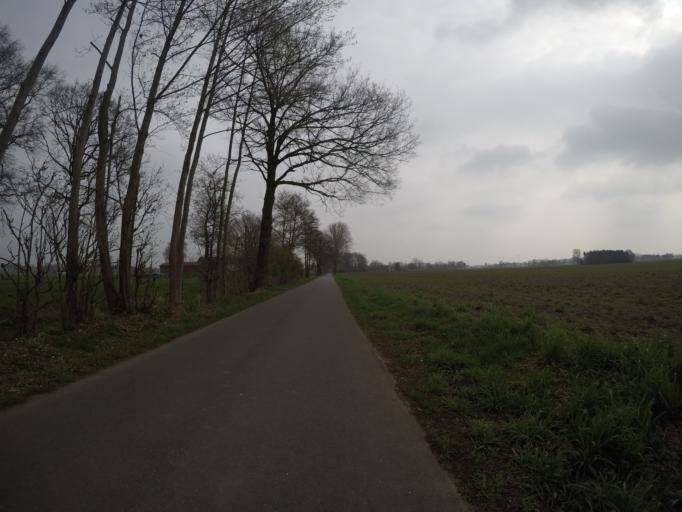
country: NL
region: Gelderland
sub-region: Gemeente Aalten
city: Aalten
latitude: 51.8748
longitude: 6.5313
